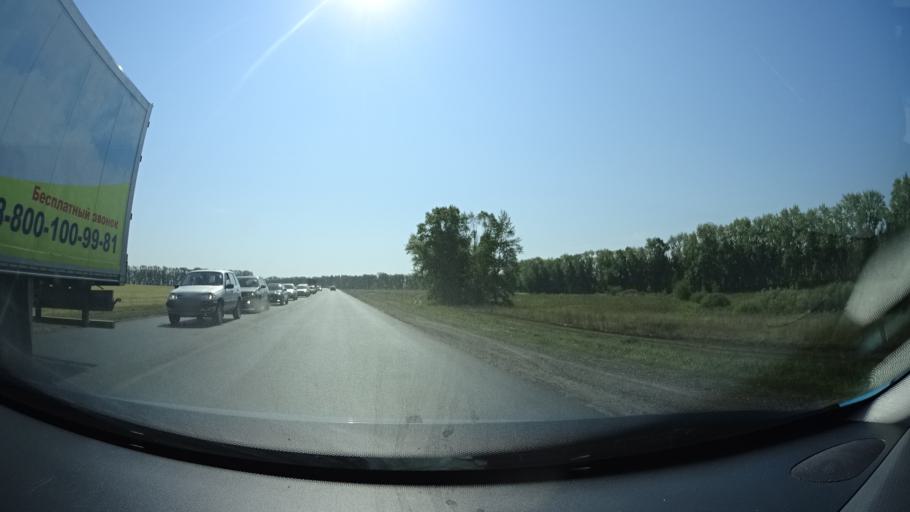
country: RU
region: Bashkortostan
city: Kabakovo
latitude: 54.4842
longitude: 55.9219
